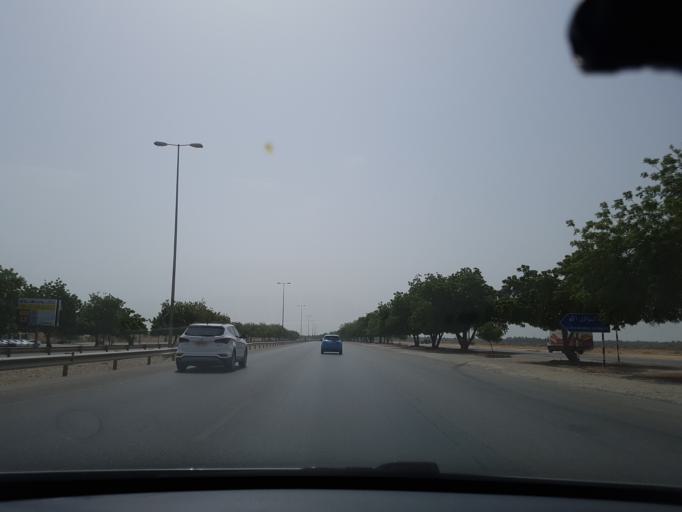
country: OM
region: Al Batinah
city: As Suwayq
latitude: 23.8092
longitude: 57.4644
